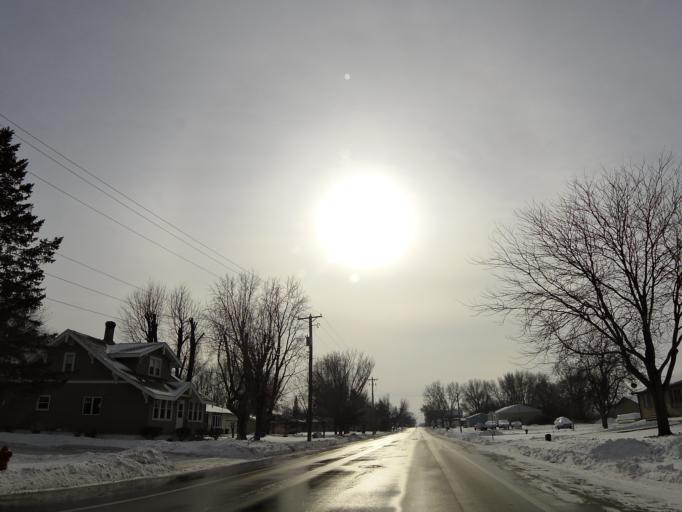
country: US
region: Minnesota
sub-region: McLeod County
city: Lester Prairie
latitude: 44.8875
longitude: -93.9703
